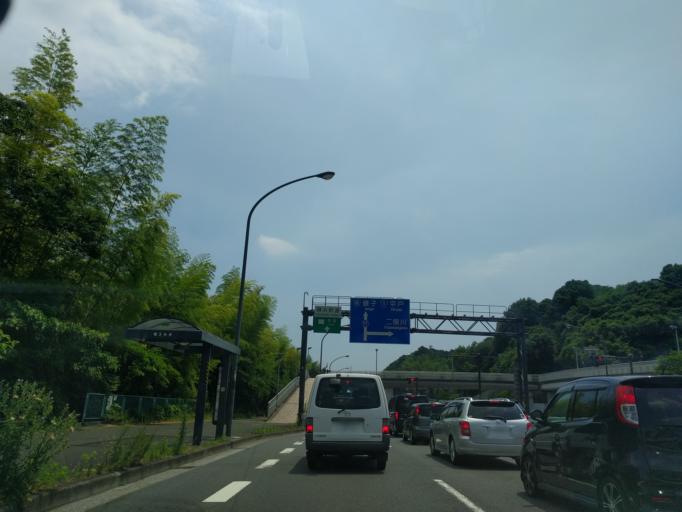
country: JP
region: Kanagawa
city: Yokohama
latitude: 35.4483
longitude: 139.5603
